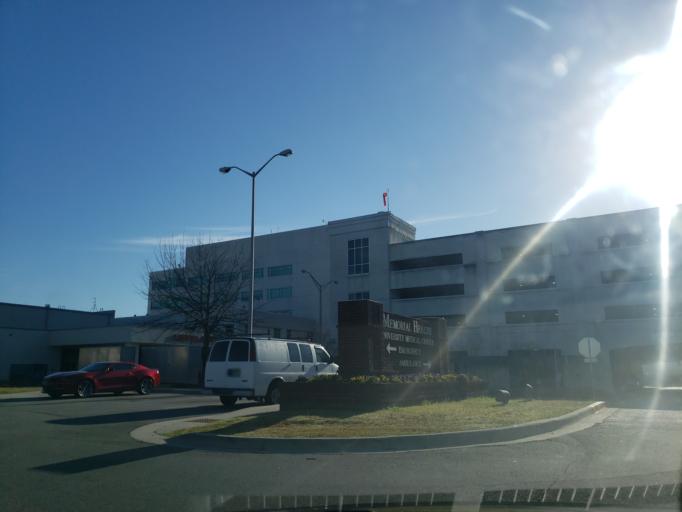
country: US
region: Georgia
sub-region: Chatham County
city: Thunderbolt
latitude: 32.0291
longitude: -81.0892
